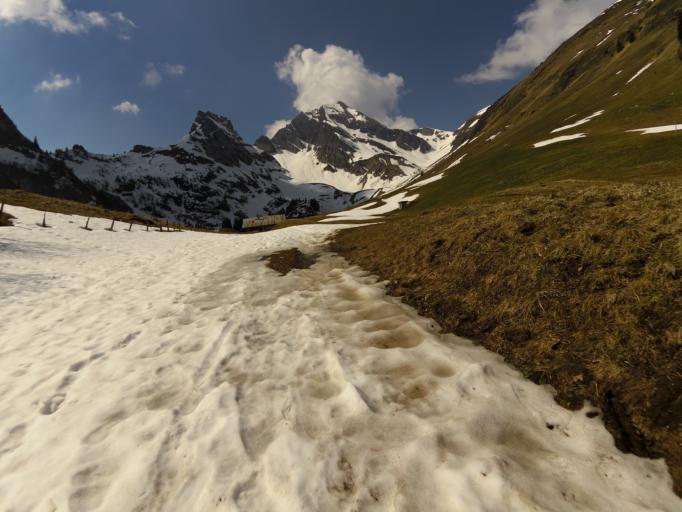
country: CH
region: Nidwalden
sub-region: Nidwalden
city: Emmetten
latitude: 46.9017
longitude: 8.4937
